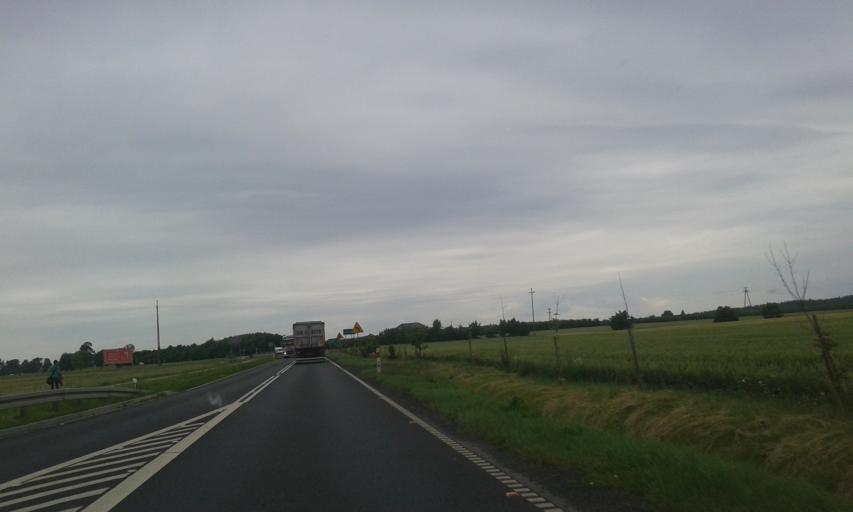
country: PL
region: Kujawsko-Pomorskie
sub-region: Powiat bydgoski
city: Koronowo
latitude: 53.2293
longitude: 17.9193
